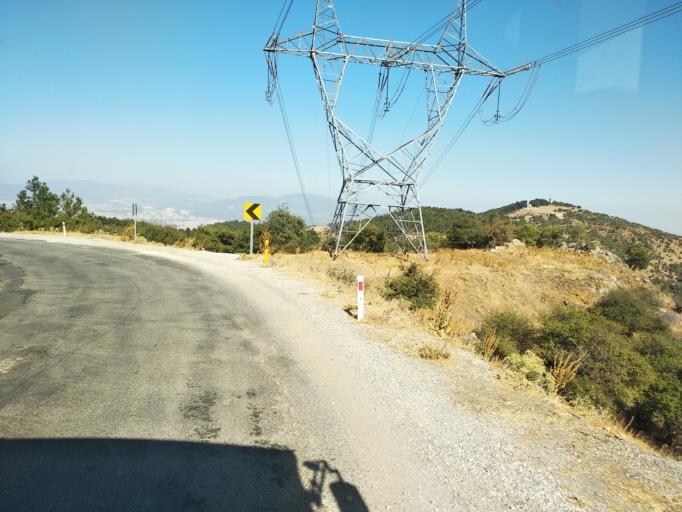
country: TR
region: Izmir
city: Gaziemir
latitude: 38.3159
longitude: 27.0092
